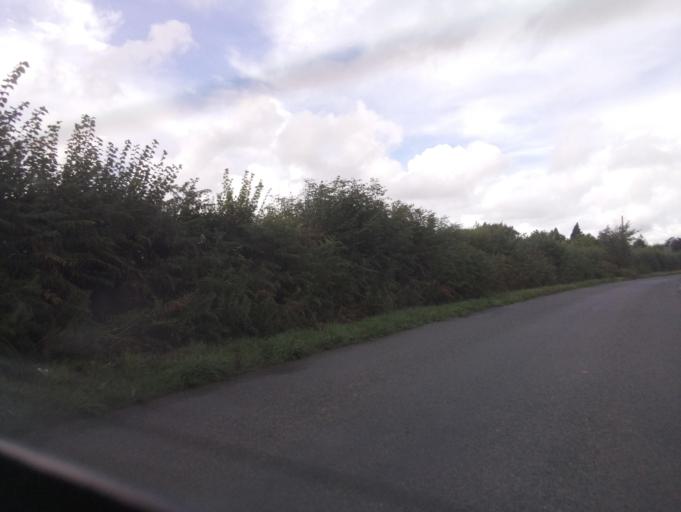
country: GB
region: England
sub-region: Worcestershire
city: Kidderminster
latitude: 52.3592
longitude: -2.1918
